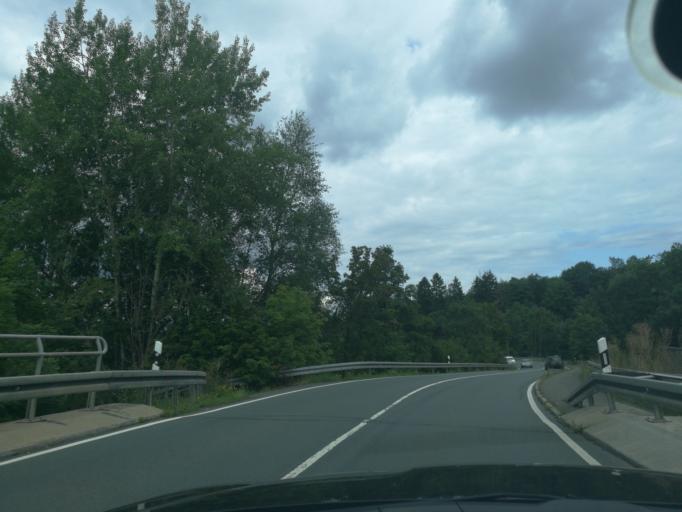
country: DE
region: Saxony
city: Adorf
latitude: 50.3507
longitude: 12.2298
